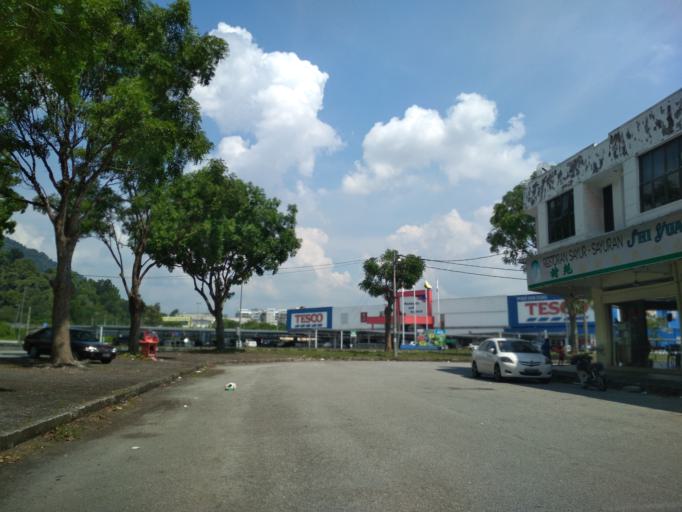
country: MY
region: Perak
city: Kampar
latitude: 4.3364
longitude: 101.1547
